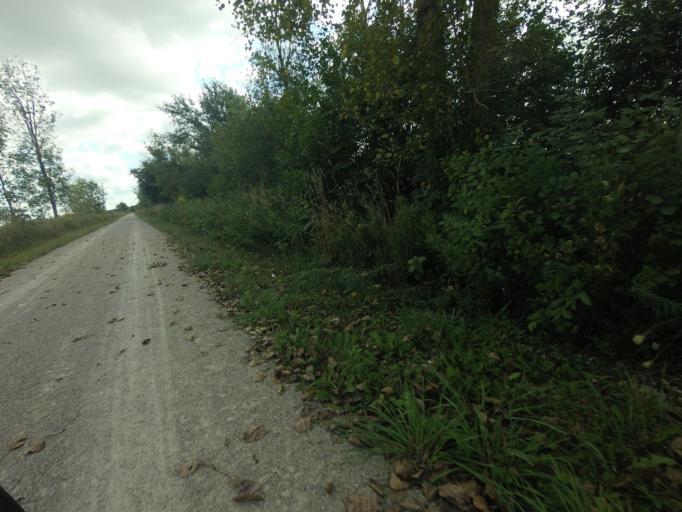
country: CA
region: Ontario
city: Huron East
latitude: 43.6056
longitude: -81.1191
